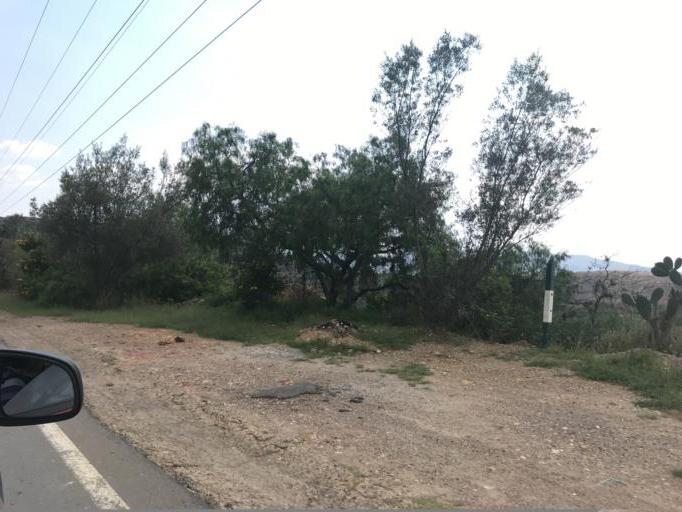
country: CO
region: Boyaca
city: Sachica
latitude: 5.6161
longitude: -73.5350
